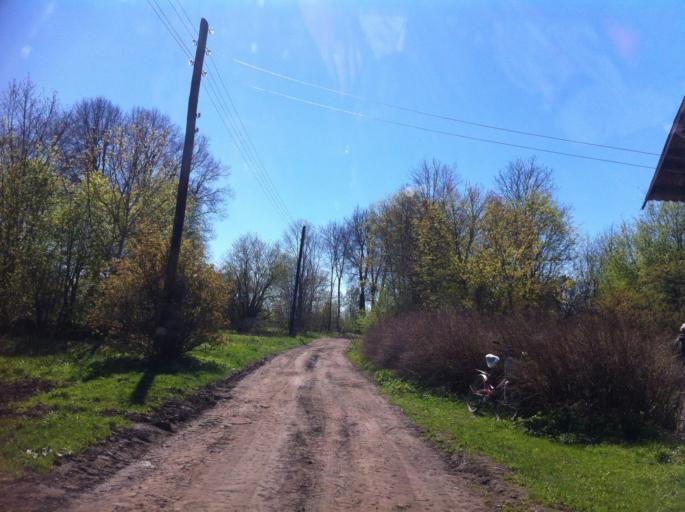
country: RU
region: Pskov
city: Izborsk
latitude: 57.7936
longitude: 27.9912
